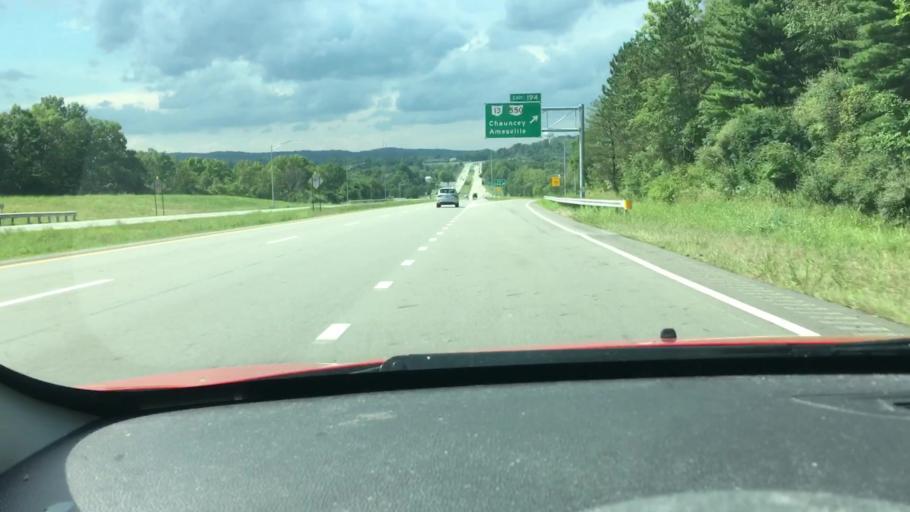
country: US
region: Ohio
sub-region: Athens County
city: Athens
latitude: 39.3588
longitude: -82.1021
